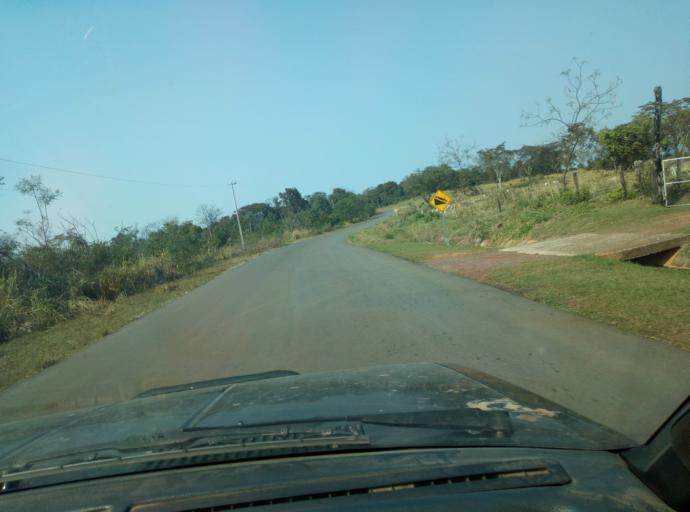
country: PY
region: Caaguazu
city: Carayao
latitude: -25.2022
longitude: -56.3075
